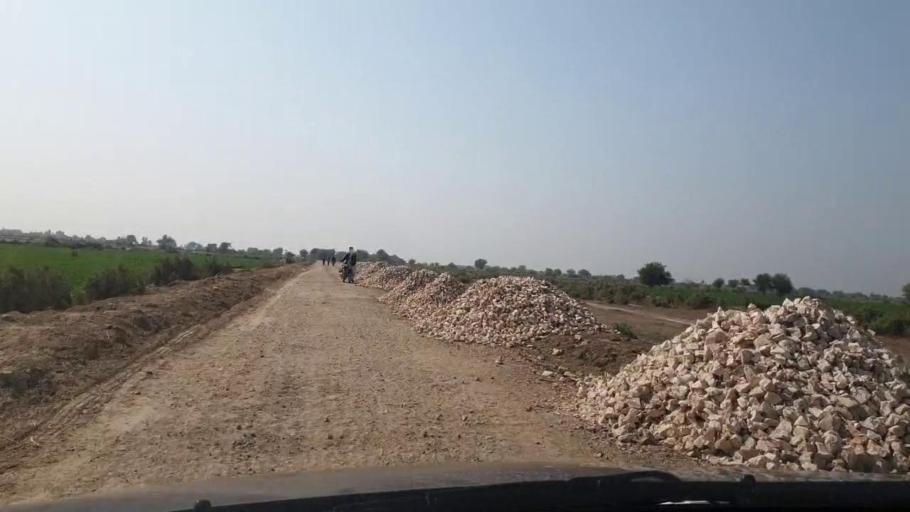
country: PK
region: Sindh
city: Jhol
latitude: 25.8883
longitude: 68.9992
